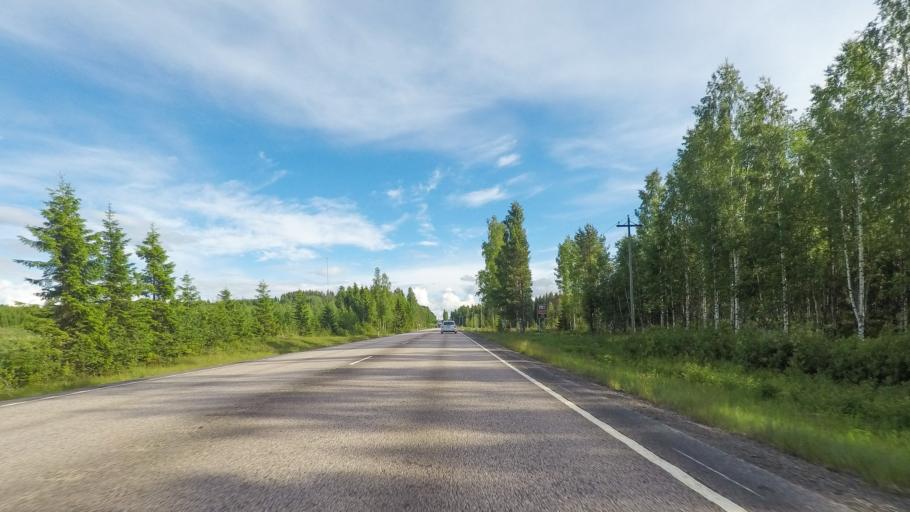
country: FI
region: Central Finland
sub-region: Joutsa
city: Leivonmaeki
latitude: 61.9316
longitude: 26.1148
